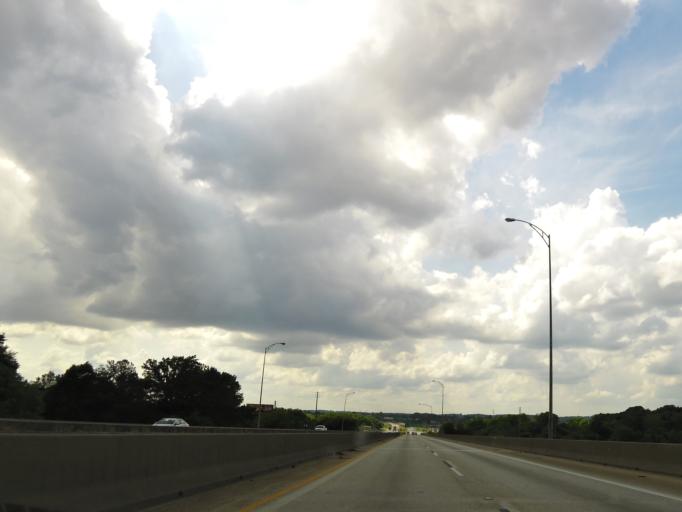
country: US
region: Alabama
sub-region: Jefferson County
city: Irondale
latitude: 33.5415
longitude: -86.7341
